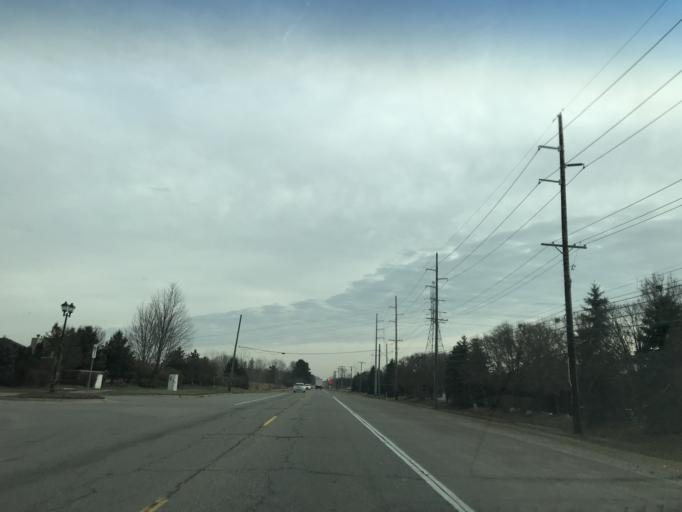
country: US
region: Michigan
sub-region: Macomb County
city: Mount Clemens
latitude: 42.6728
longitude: -82.9068
